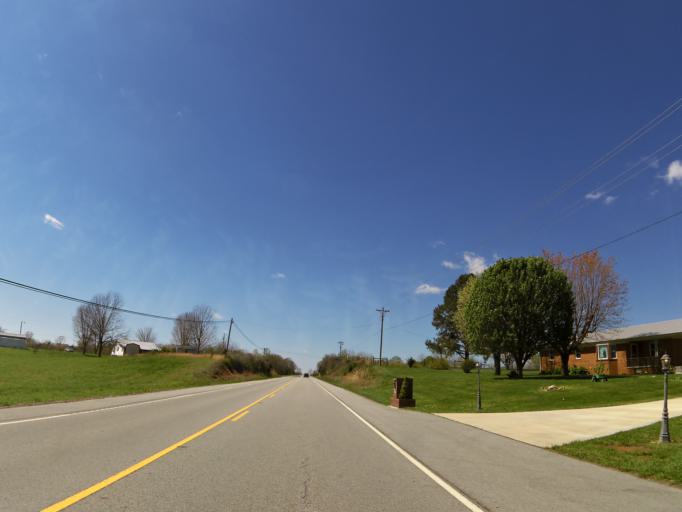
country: US
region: Tennessee
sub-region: White County
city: Sparta
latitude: 35.9607
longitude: -85.6154
